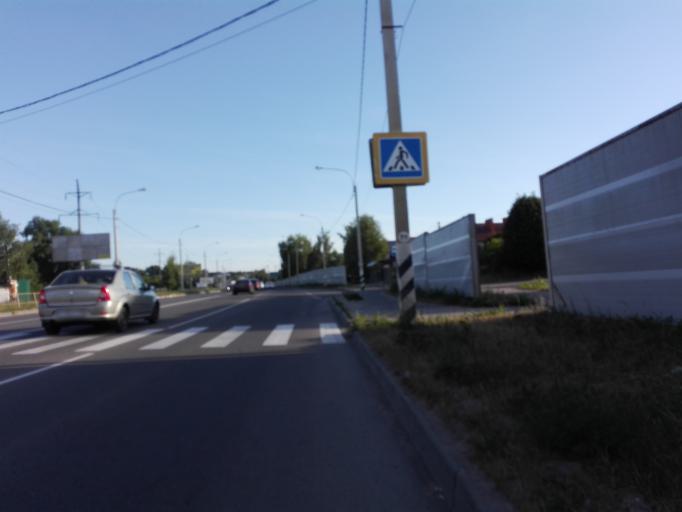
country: RU
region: Orjol
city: Orel
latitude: 52.9566
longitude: 36.0307
